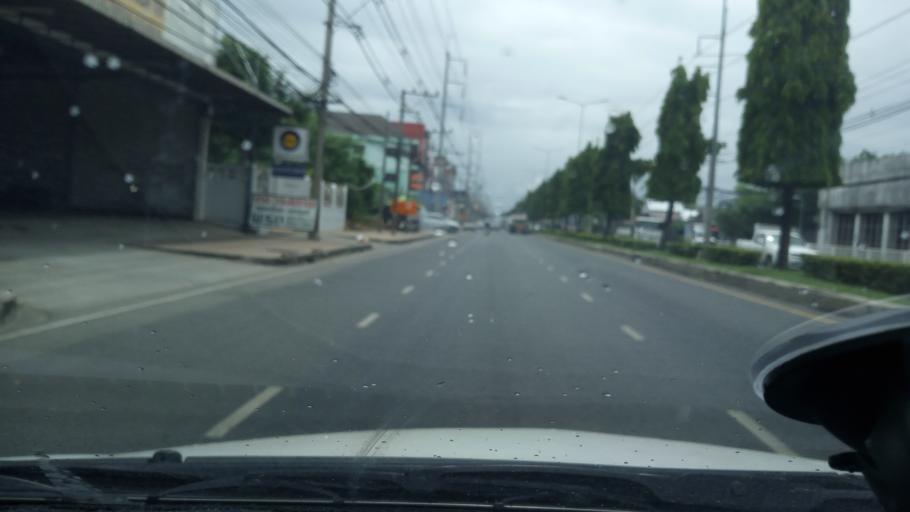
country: TH
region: Chon Buri
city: Phanat Nikhom
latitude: 13.4542
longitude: 101.1748
